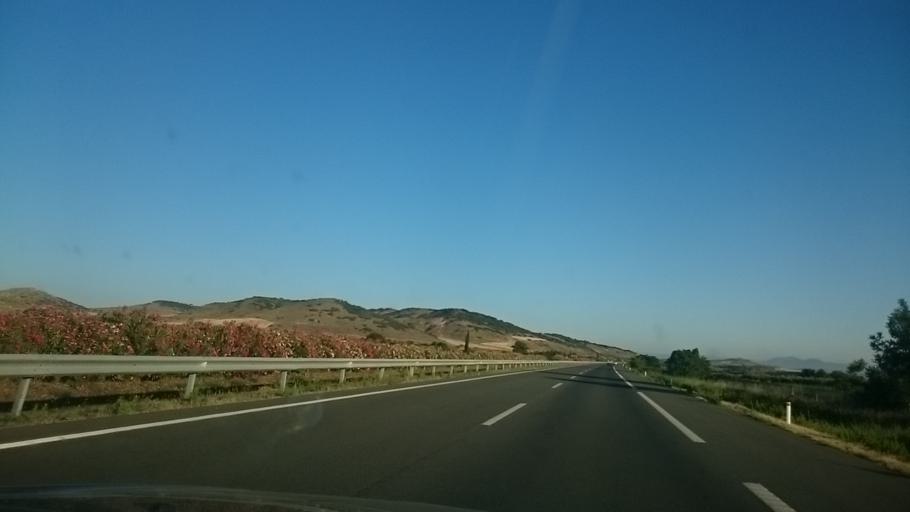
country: ES
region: La Rioja
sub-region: Provincia de La Rioja
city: Pradejon
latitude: 42.3478
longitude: -2.0479
